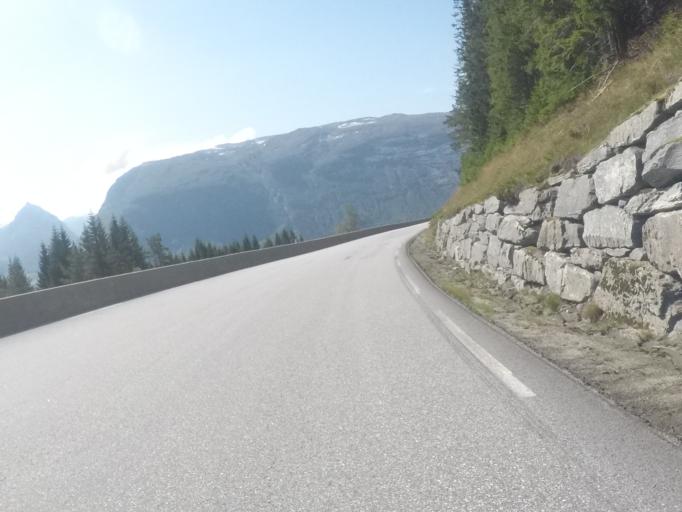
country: NO
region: Sogn og Fjordane
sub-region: Jolster
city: Skei
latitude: 61.7590
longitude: 6.5001
